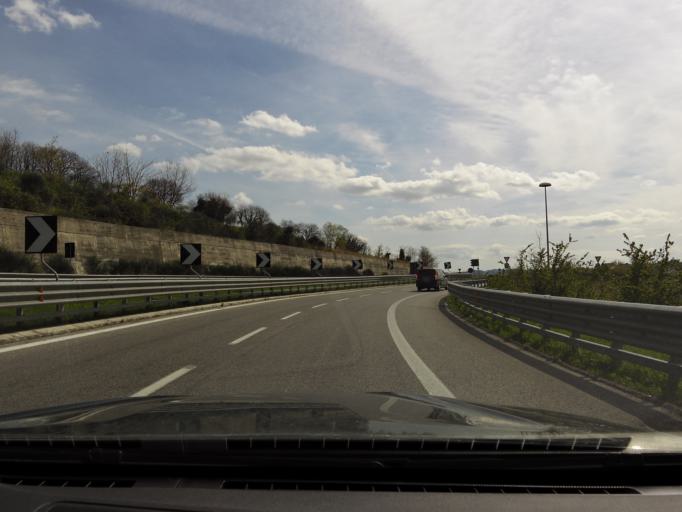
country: IT
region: The Marches
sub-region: Provincia di Ancona
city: San Biagio
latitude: 43.5370
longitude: 13.5184
